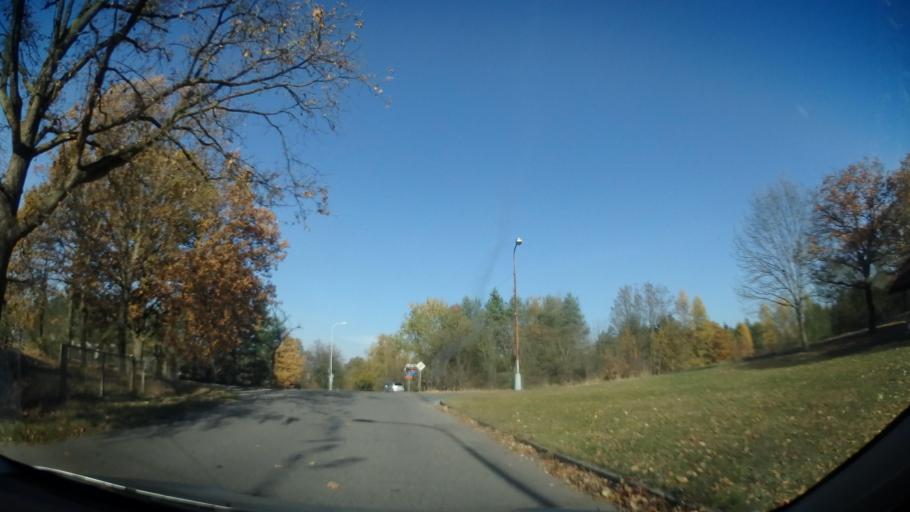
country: CZ
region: Kralovehradecky
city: Trebechovice pod Orebem
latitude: 50.1997
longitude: 16.0057
